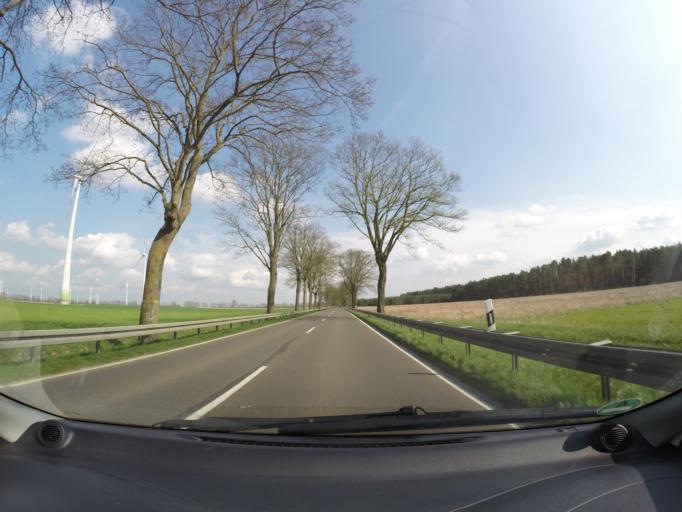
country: DE
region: Brandenburg
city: Rehfelde
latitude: 52.4804
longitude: 13.9263
